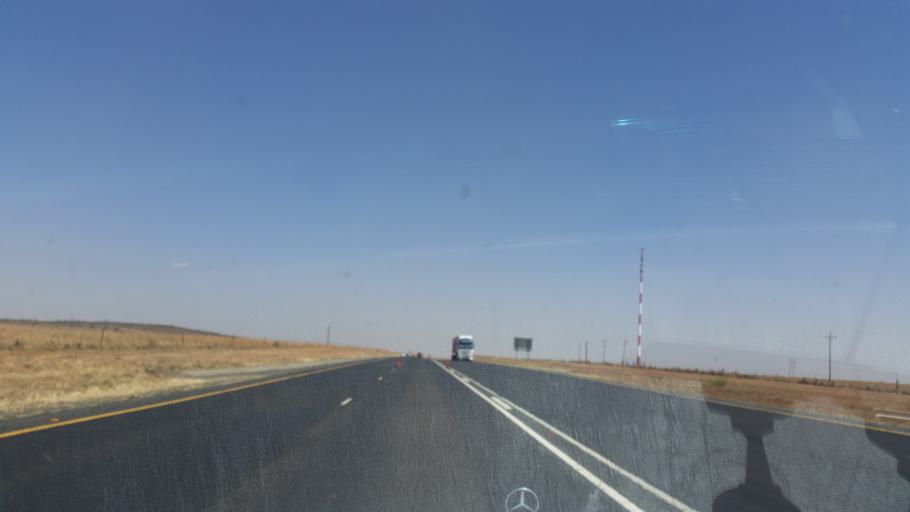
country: ZA
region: Orange Free State
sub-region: Lejweleputswa District Municipality
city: Brandfort
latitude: -28.8111
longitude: 26.6743
